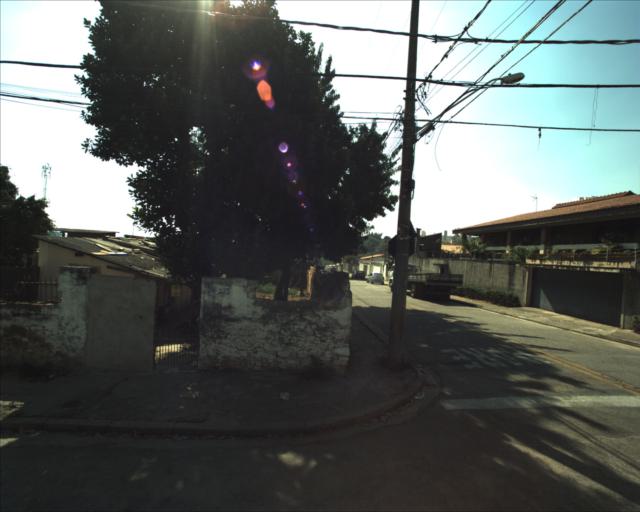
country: BR
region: Sao Paulo
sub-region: Sorocaba
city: Sorocaba
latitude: -23.5013
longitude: -47.4321
